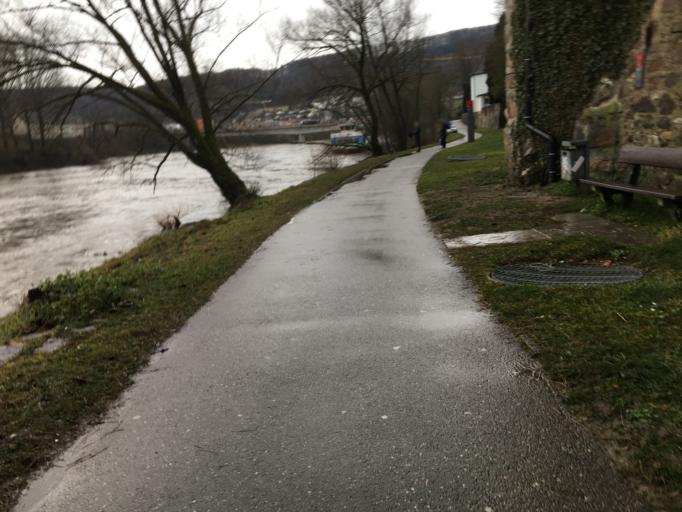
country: DE
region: Baden-Wuerttemberg
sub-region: Freiburg Region
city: Bad Sackingen
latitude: 47.5505
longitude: 7.9500
